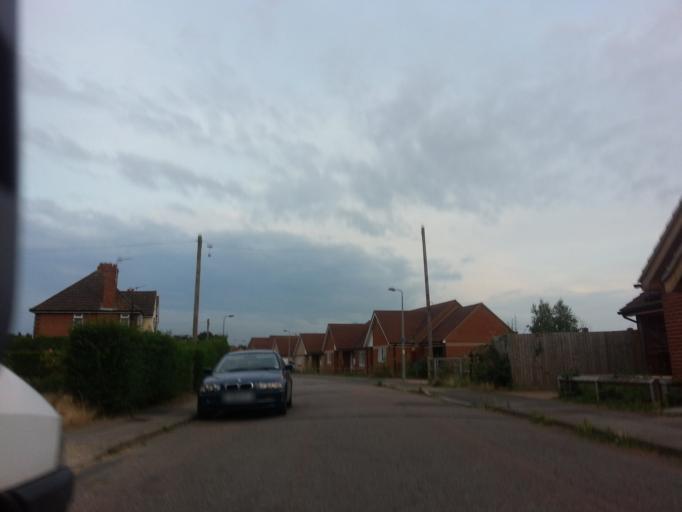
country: GB
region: England
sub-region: Suffolk
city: Ipswich
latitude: 52.0308
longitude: 1.1757
